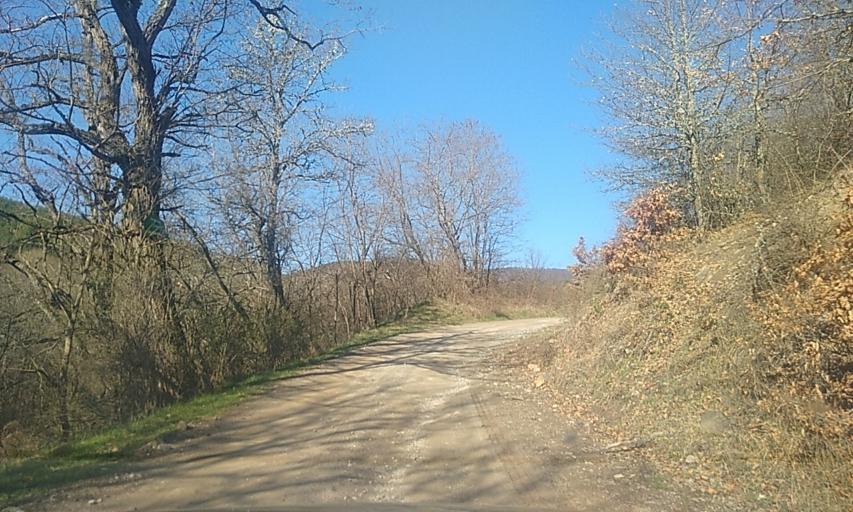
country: RS
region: Central Serbia
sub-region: Pcinjski Okrug
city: Bosilegrad
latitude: 42.3582
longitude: 22.4144
